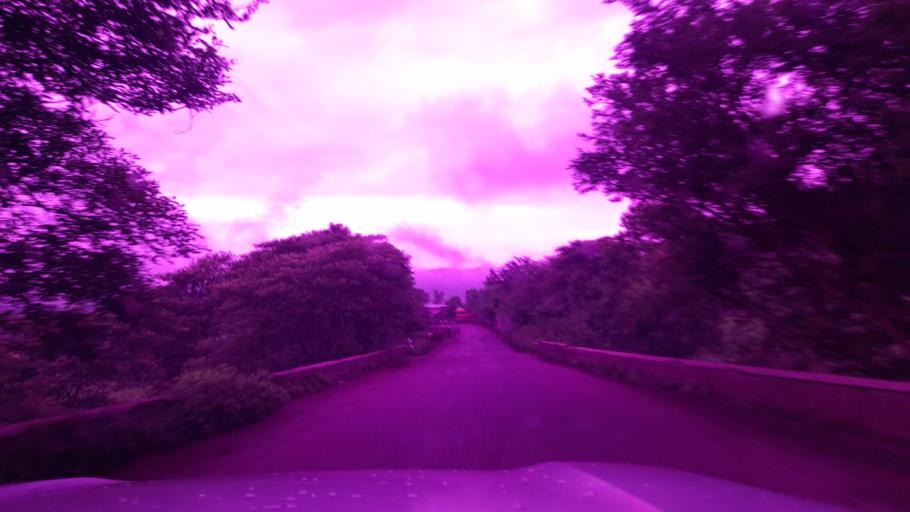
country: ET
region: Oromiya
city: Waliso
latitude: 8.2254
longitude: 37.5754
